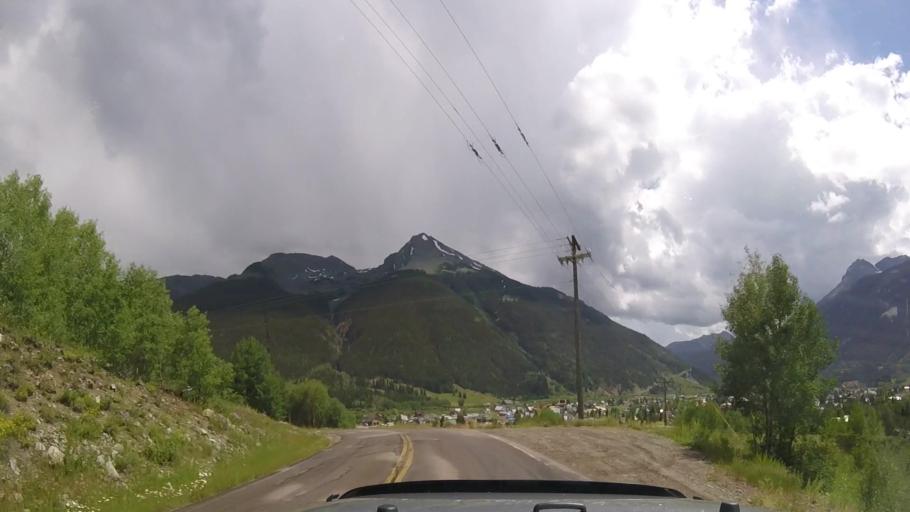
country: US
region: Colorado
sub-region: San Juan County
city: Silverton
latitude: 37.8198
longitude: -107.6607
